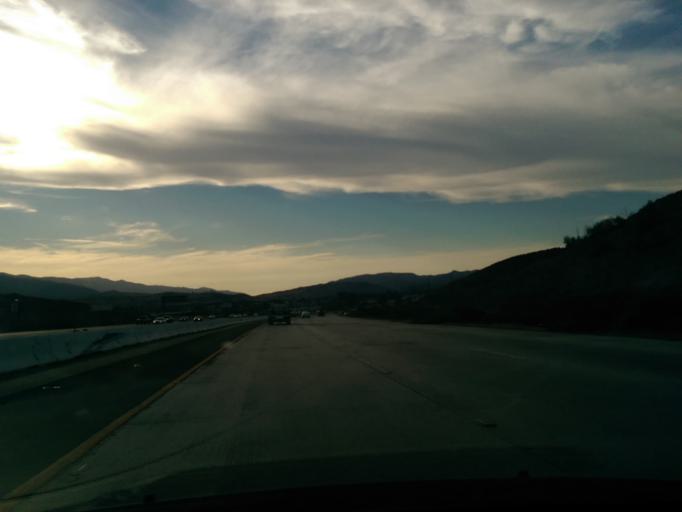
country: US
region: California
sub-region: Riverside County
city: Lake Elsinore
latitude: 33.6760
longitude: -117.3215
